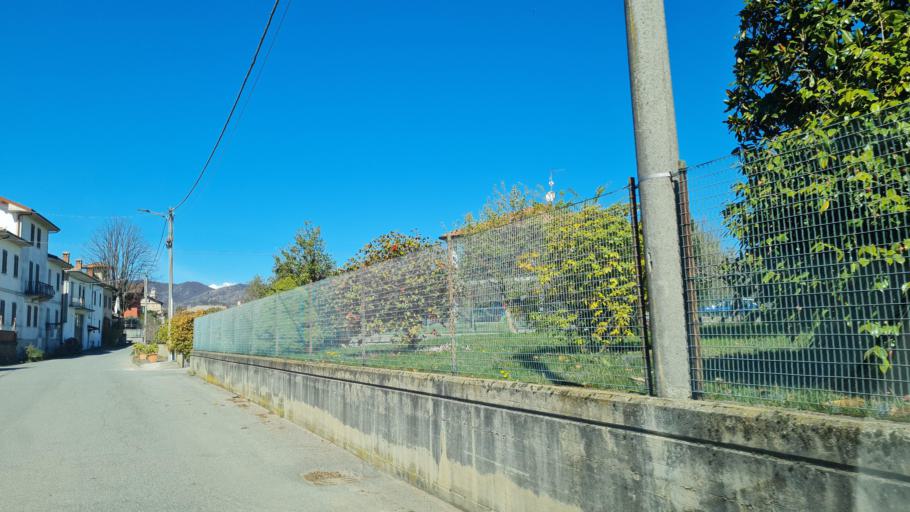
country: IT
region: Piedmont
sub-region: Provincia di Novara
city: Maggiora
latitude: 45.6878
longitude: 8.4304
